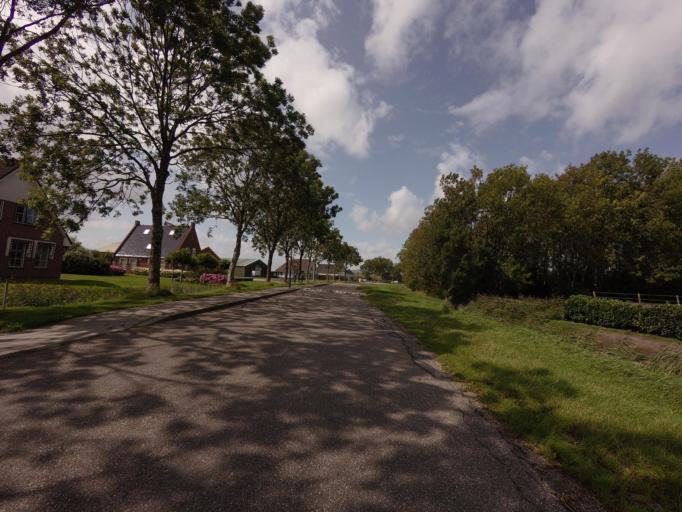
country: NL
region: Friesland
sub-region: Gemeente Harlingen
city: Harlingen
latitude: 53.1484
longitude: 5.4795
